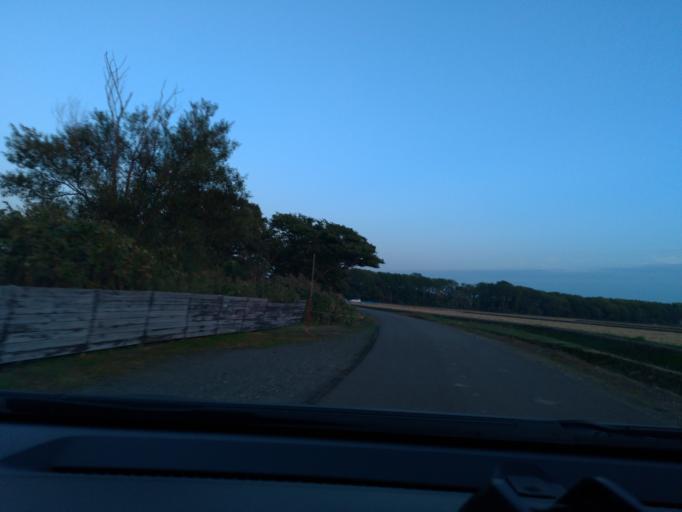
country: JP
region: Hokkaido
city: Iwamizawa
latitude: 43.3298
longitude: 141.7105
